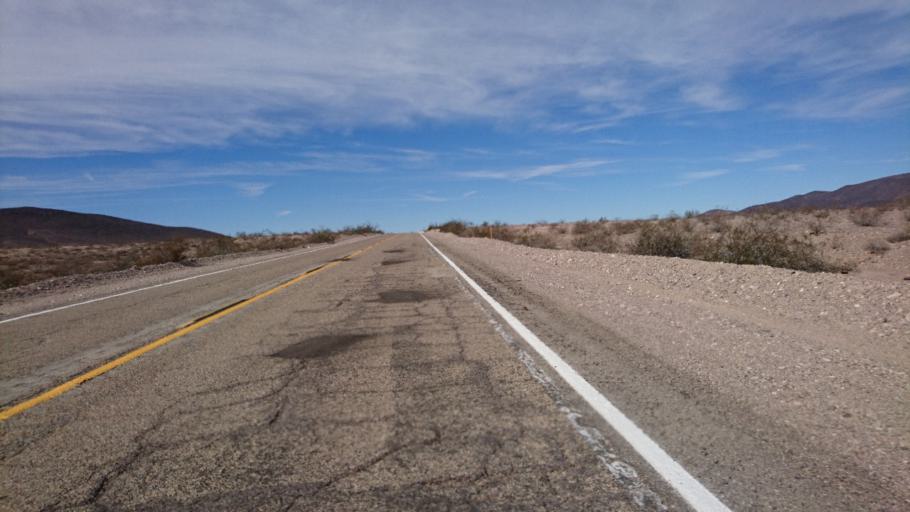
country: US
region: California
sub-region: San Bernardino County
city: Twentynine Palms
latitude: 34.6940
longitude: -116.0514
